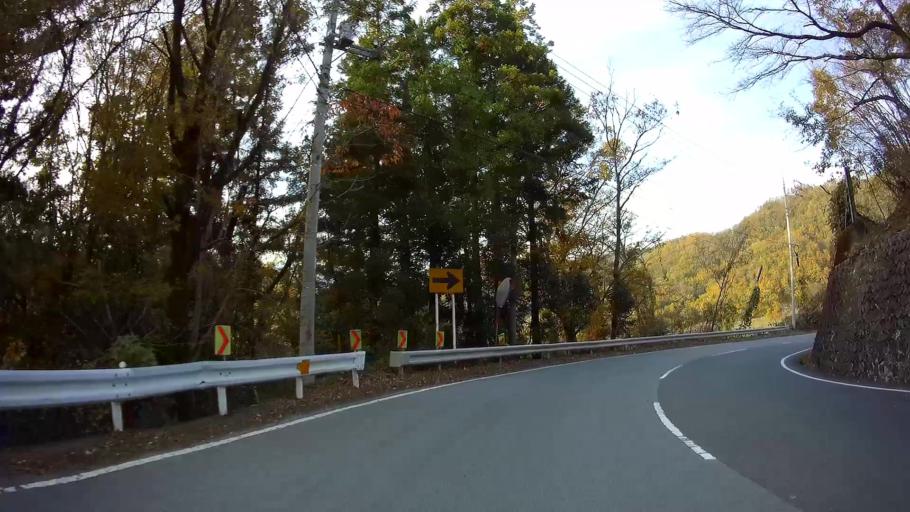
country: JP
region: Yamanashi
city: Ryuo
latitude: 35.4785
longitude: 138.4869
